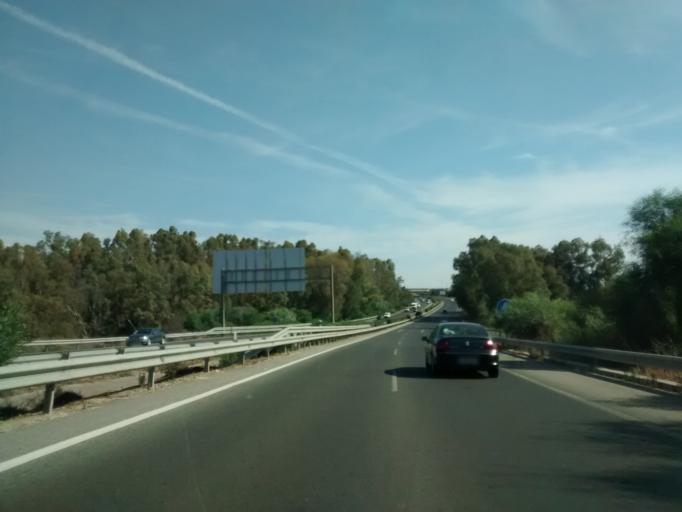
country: ES
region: Andalusia
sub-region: Provincia de Cadiz
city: Chiclana de la Frontera
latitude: 36.4189
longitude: -6.1173
